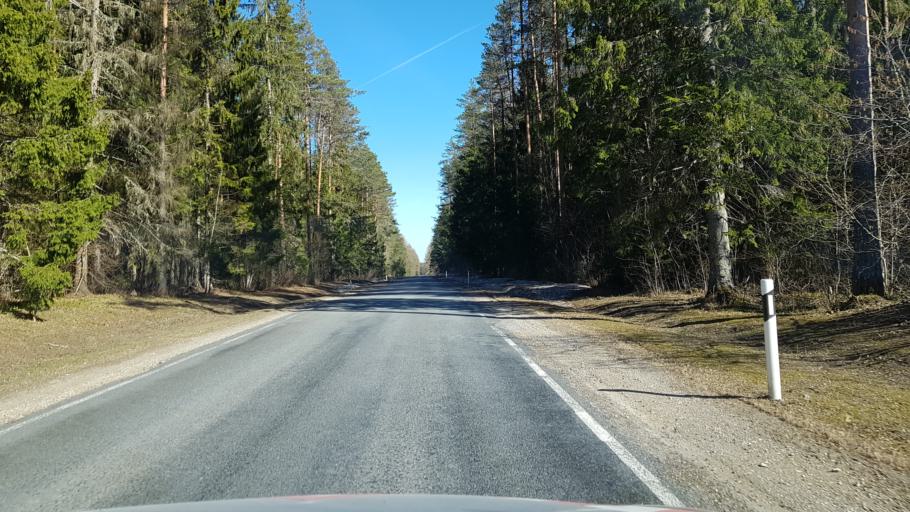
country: EE
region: Laeaene-Virumaa
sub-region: Vinni vald
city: Vinni
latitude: 59.2738
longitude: 26.6226
